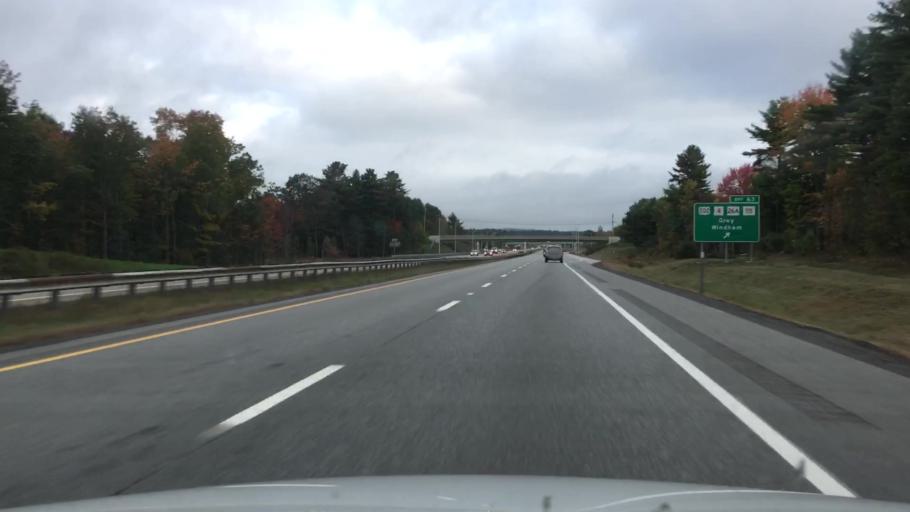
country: US
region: Maine
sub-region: Cumberland County
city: New Gloucester
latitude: 43.8759
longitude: -70.3315
